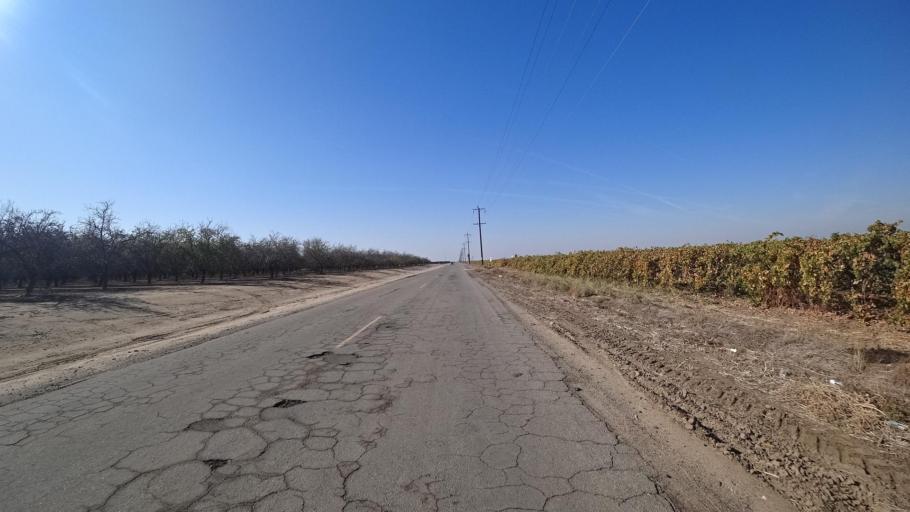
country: US
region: California
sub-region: Kern County
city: McFarland
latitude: 35.7035
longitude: -119.1623
